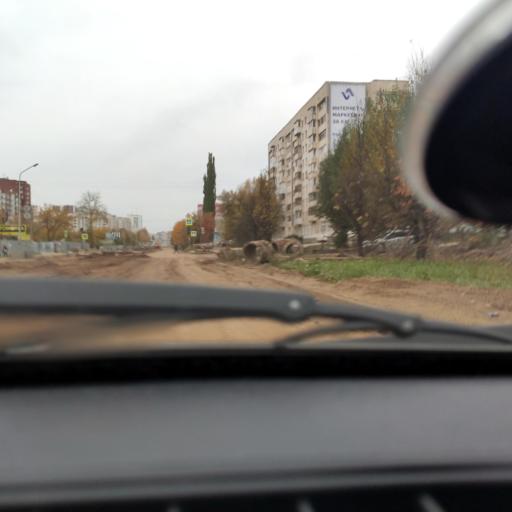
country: RU
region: Bashkortostan
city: Ufa
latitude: 54.7475
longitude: 56.0008
